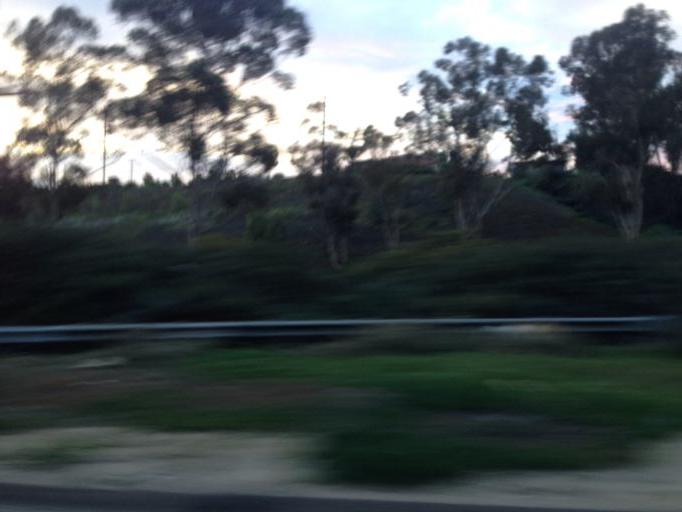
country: US
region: California
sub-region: San Diego County
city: San Diego
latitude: 32.7382
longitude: -117.1151
